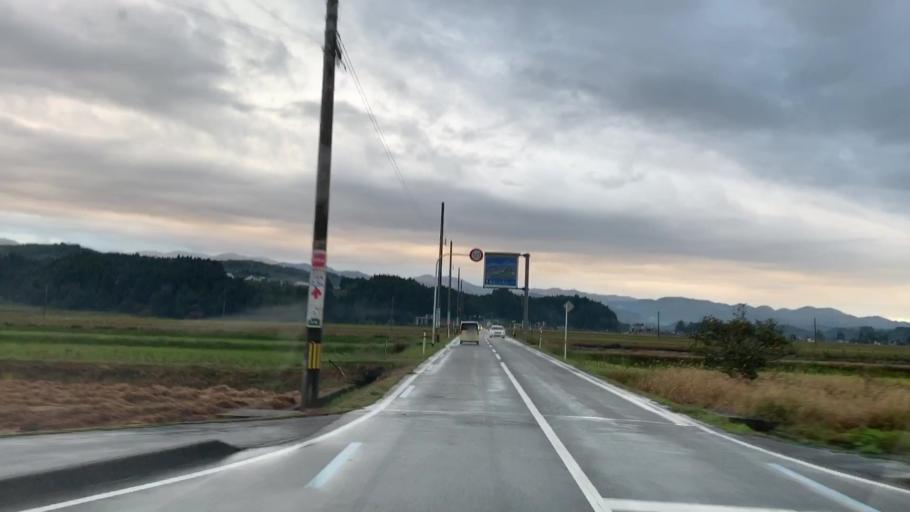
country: JP
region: Toyama
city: Kamiichi
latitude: 36.6254
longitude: 137.3286
